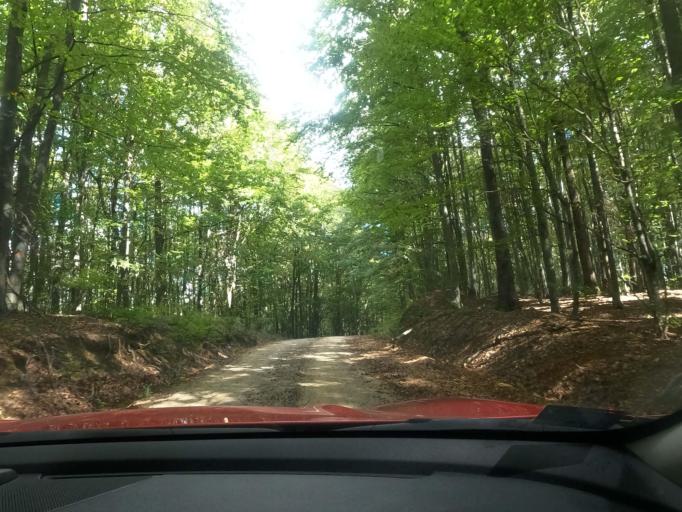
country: BA
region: Federation of Bosnia and Herzegovina
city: Velika Kladusa
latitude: 45.2612
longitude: 15.7769
